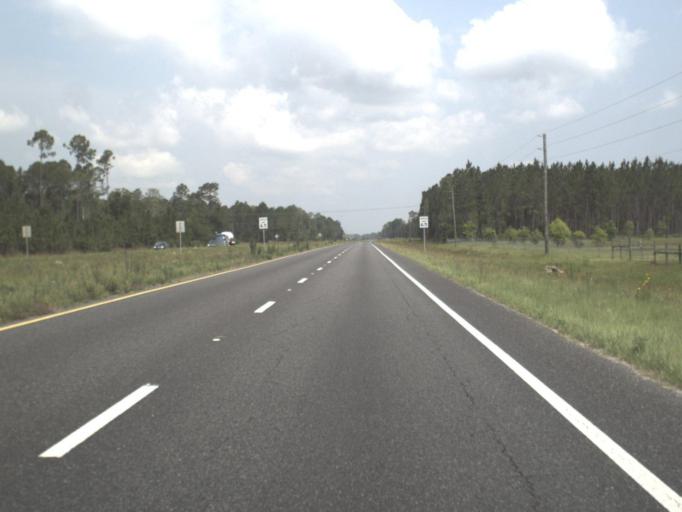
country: US
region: Florida
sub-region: Levy County
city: Bronson
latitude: 29.4540
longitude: -82.6513
